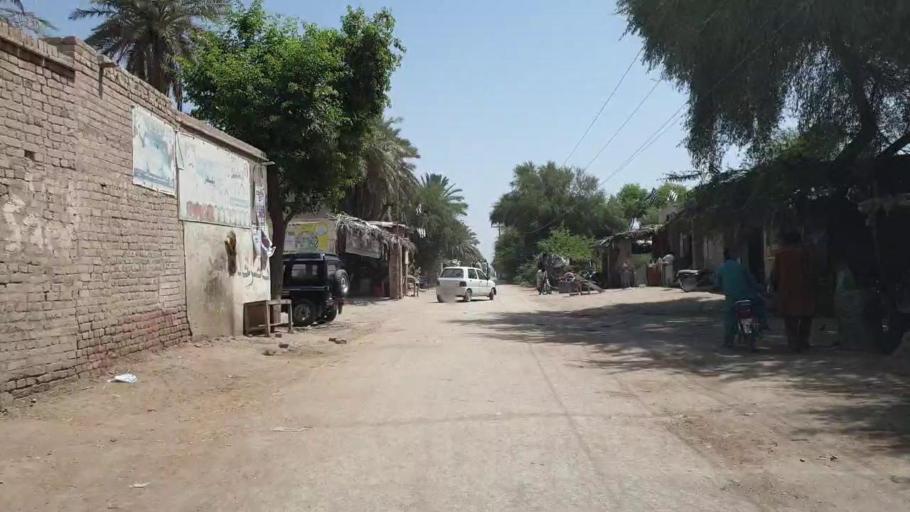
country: PK
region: Sindh
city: Adilpur
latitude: 27.8271
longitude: 69.2504
